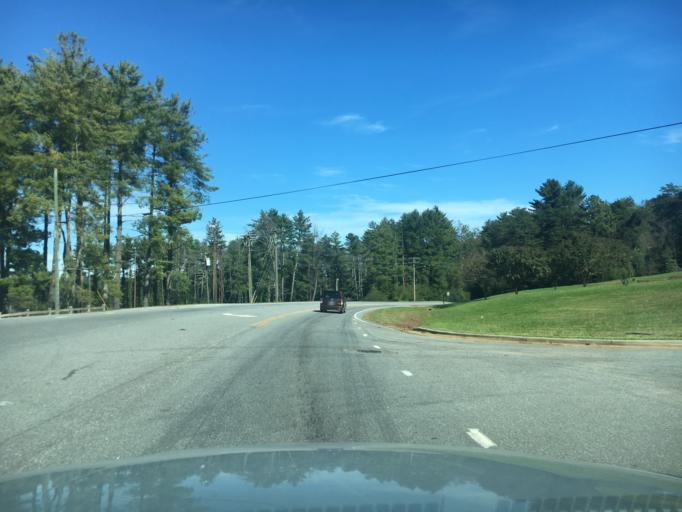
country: US
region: North Carolina
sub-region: Burke County
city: Morganton
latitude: 35.7588
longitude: -81.7030
